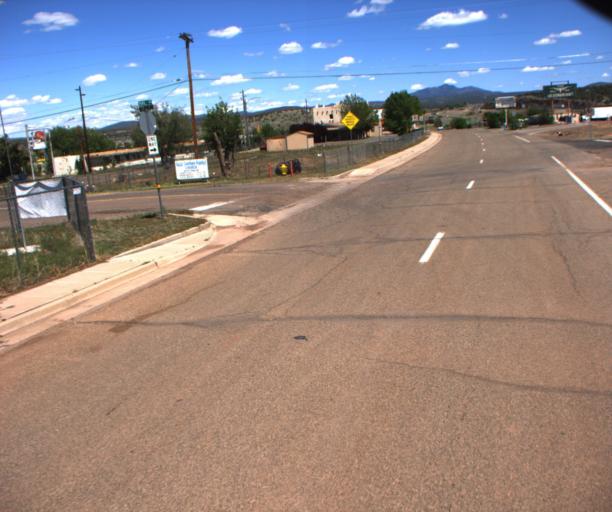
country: US
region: Arizona
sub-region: Coconino County
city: Williams
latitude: 35.2229
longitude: -112.4814
